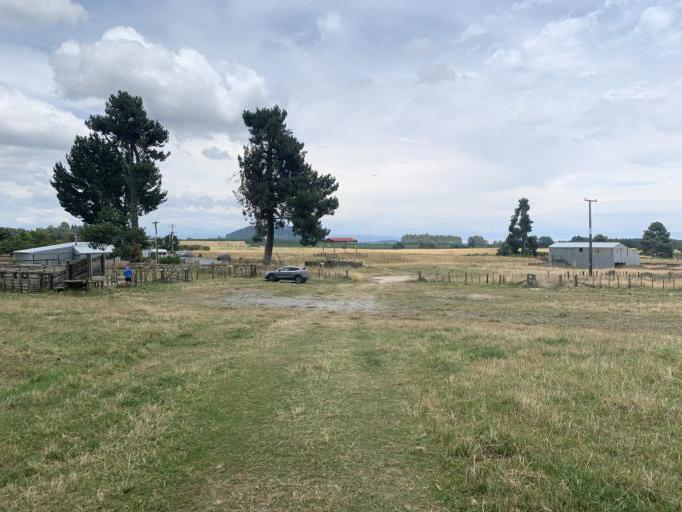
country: NZ
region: Waikato
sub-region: Taupo District
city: Taupo
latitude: -38.7039
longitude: 176.1405
